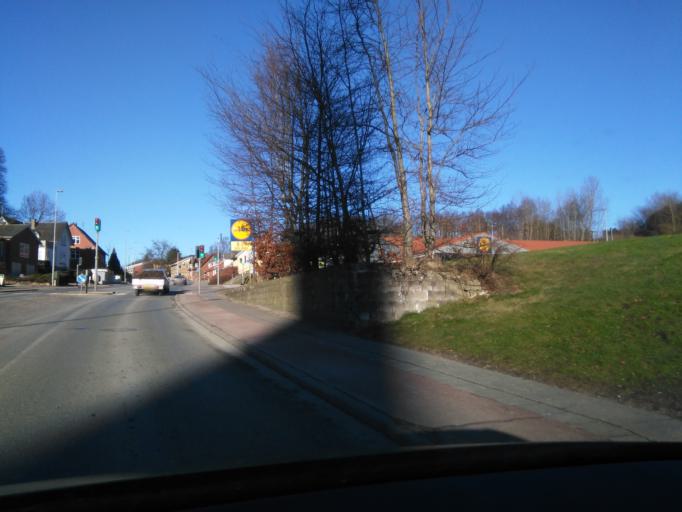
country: DK
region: North Denmark
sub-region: Mariagerfjord Kommune
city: Hobro
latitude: 56.6449
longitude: 9.7929
